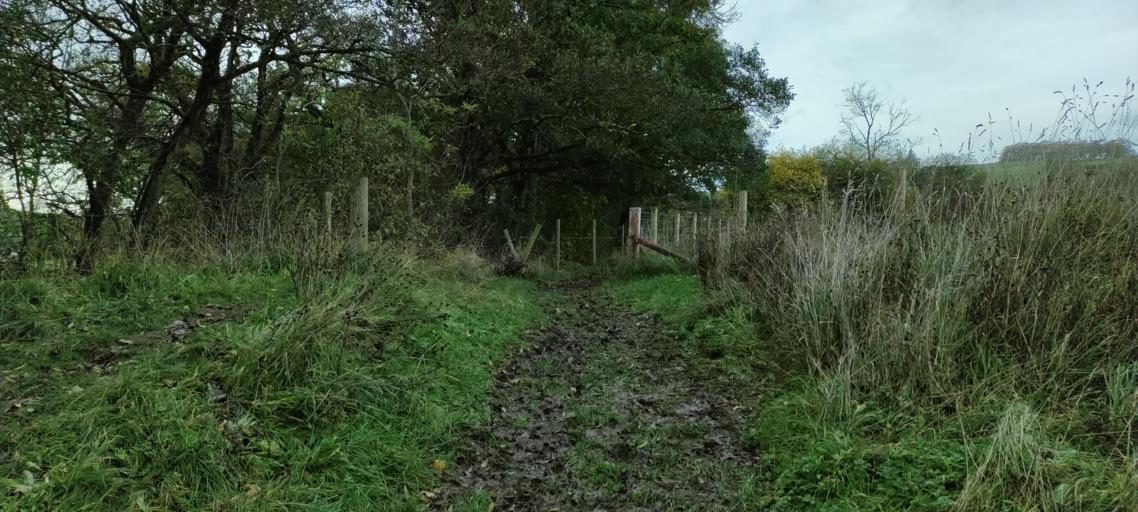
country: GB
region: England
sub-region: Cumbria
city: Wigton
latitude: 54.7485
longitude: -3.0656
